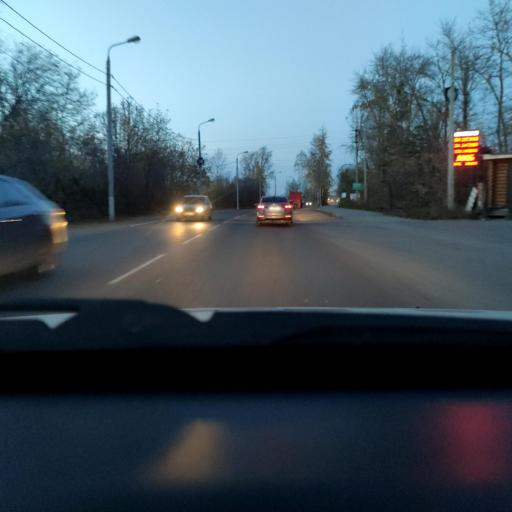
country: RU
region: Perm
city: Kondratovo
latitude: 57.9718
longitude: 56.1280
